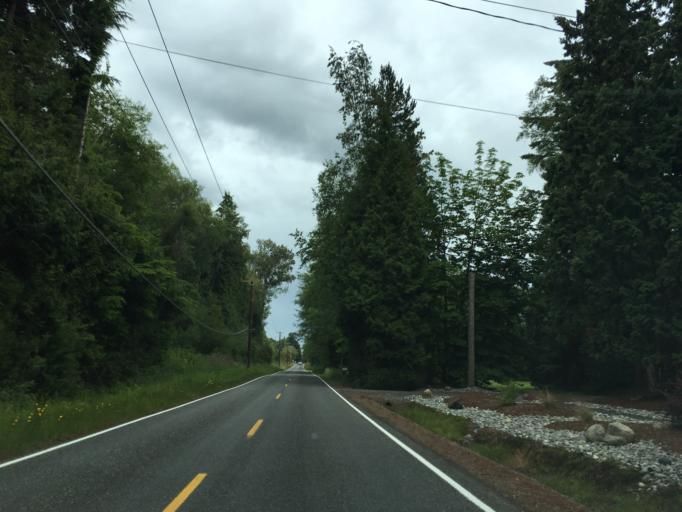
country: US
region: Washington
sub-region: Whatcom County
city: Birch Bay
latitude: 48.9433
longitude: -122.7537
